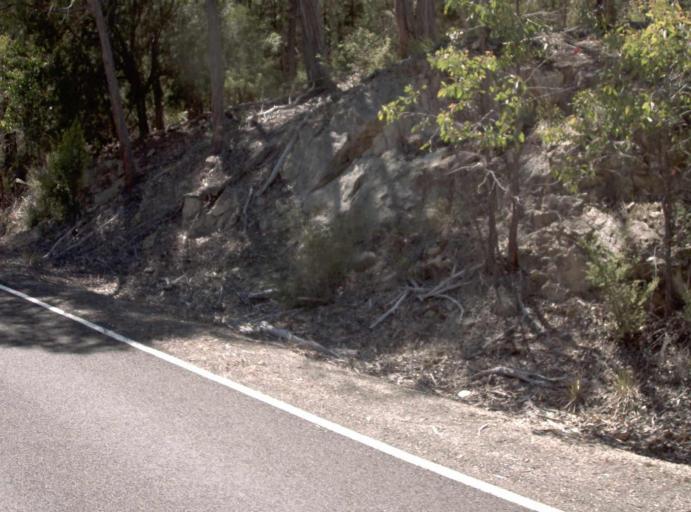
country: AU
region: Victoria
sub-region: East Gippsland
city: Lakes Entrance
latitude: -37.3724
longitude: 148.2197
